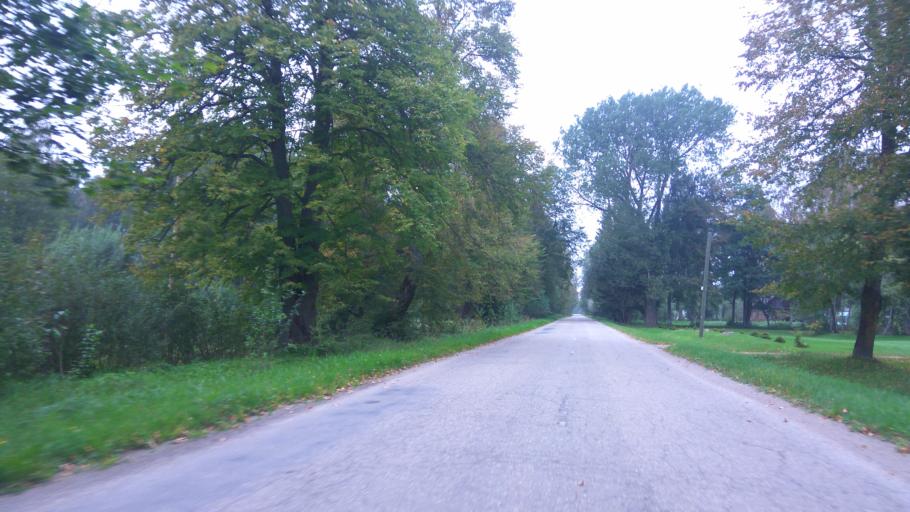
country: LV
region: Rucavas
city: Rucava
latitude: 56.1672
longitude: 21.1602
